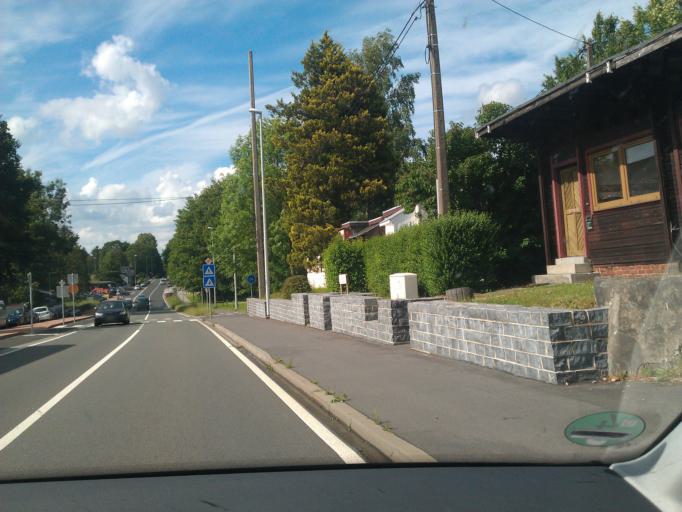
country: DE
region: North Rhine-Westphalia
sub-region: Regierungsbezirk Koln
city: Aachen
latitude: 50.7210
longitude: 6.0904
